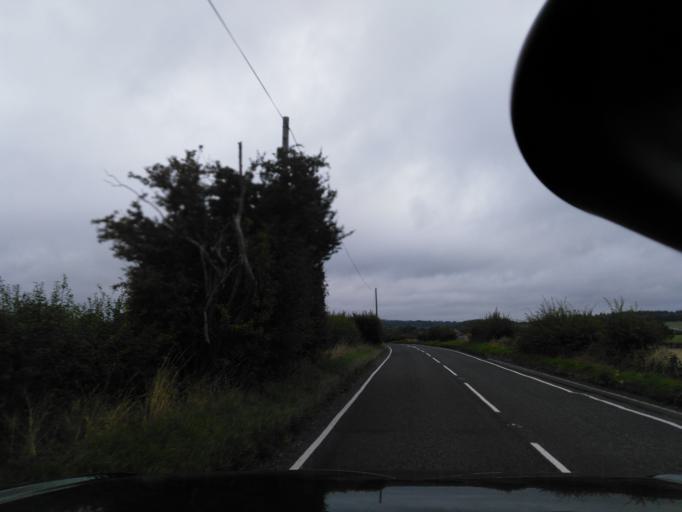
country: GB
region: England
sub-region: Wiltshire
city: Bishopstrow
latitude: 51.1601
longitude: -2.1786
